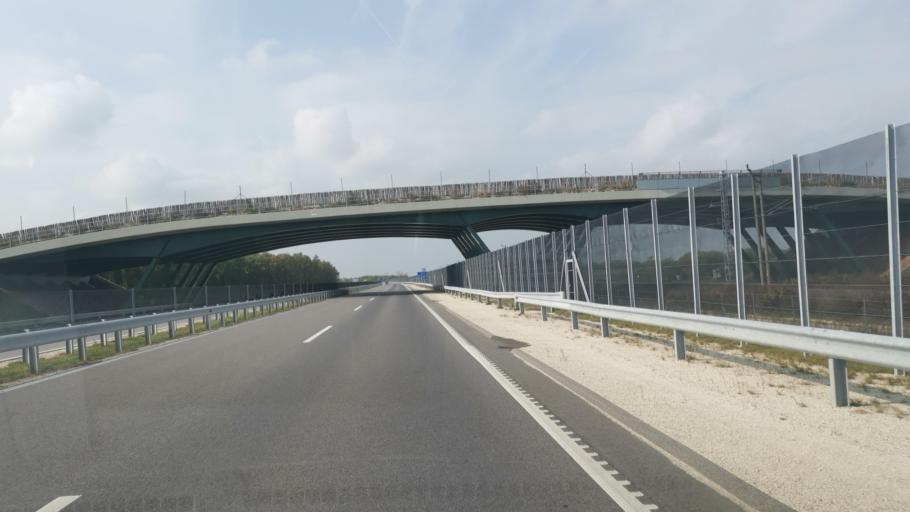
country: HU
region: Gyor-Moson-Sopron
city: Kapuvar
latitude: 47.5860
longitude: 16.9570
